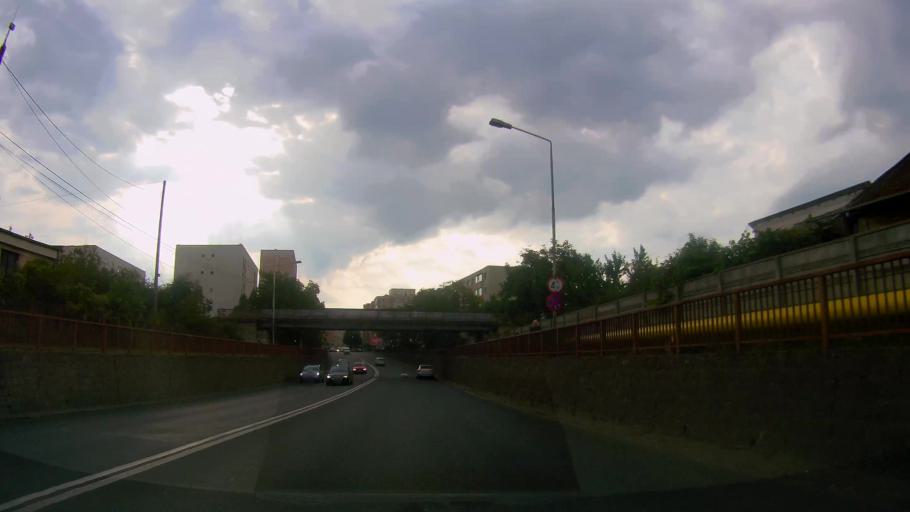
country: RO
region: Satu Mare
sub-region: Municipiul Satu Mare
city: Satu Mare
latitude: 47.7817
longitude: 22.8783
